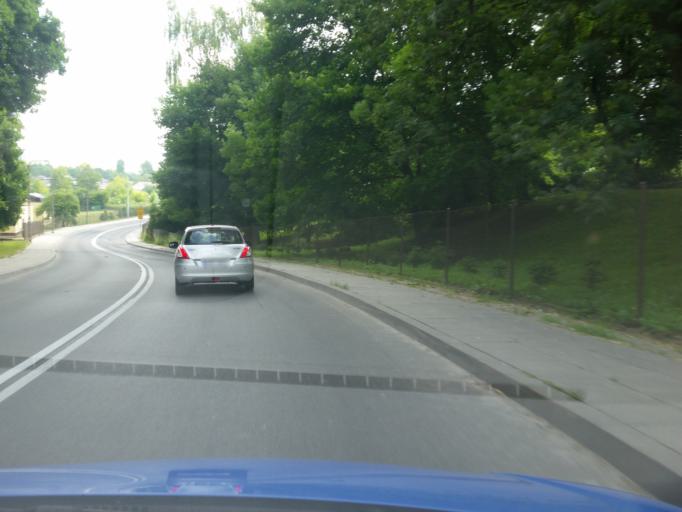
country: PL
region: Lesser Poland Voivodeship
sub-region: Powiat miechowski
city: Miechow
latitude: 50.3553
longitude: 20.0372
